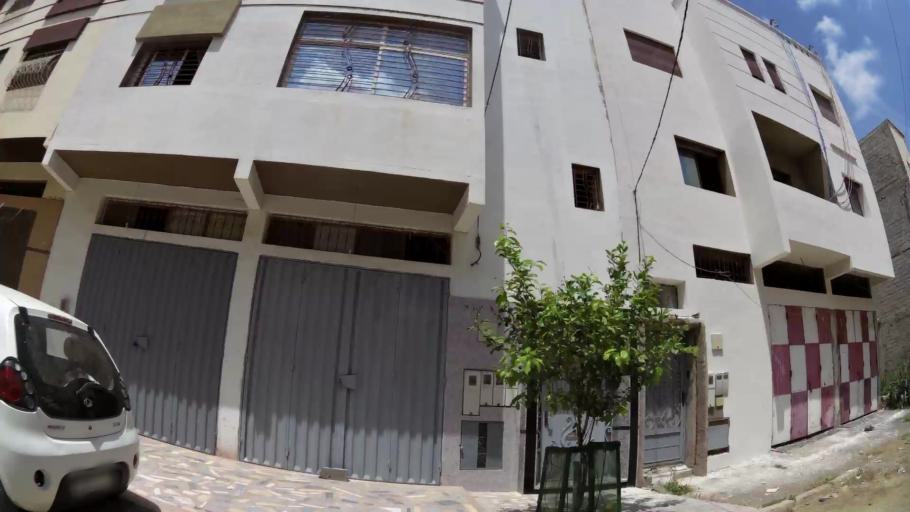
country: MA
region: Gharb-Chrarda-Beni Hssen
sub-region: Kenitra Province
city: Kenitra
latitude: 34.0098
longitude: -6.5387
